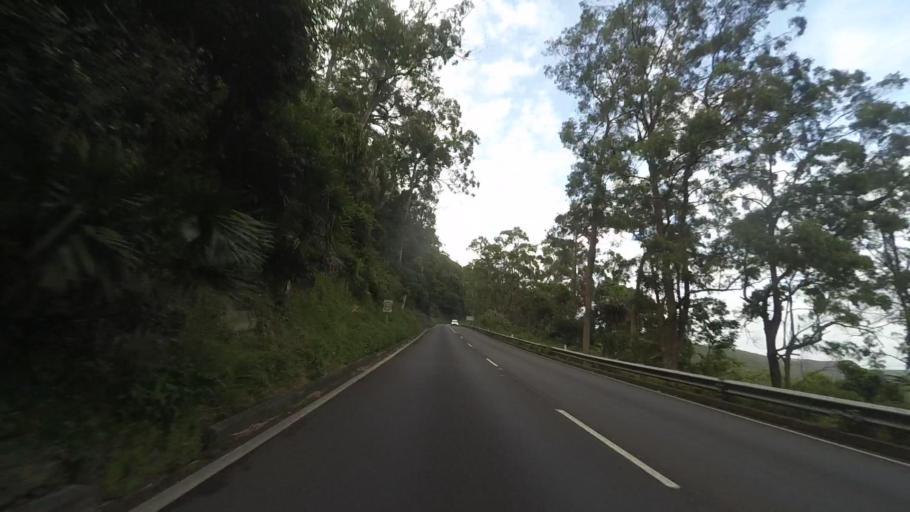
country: AU
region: New South Wales
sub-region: Wollongong
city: Bulli
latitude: -34.3215
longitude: 150.8930
